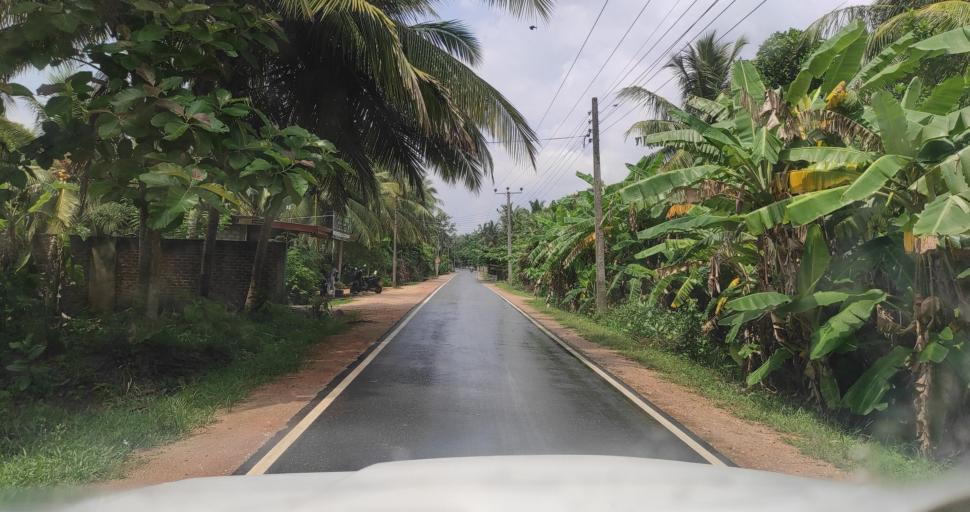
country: LK
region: Eastern Province
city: Trincomalee
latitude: 8.3741
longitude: 81.0094
